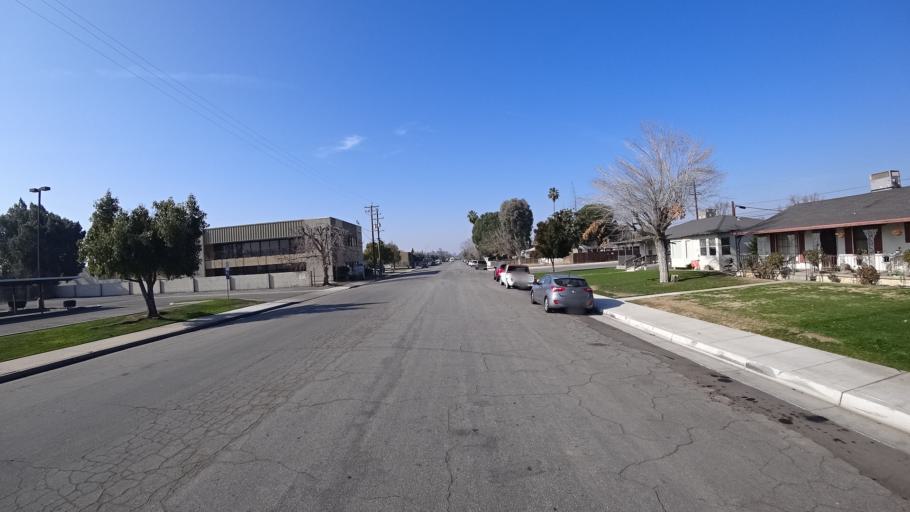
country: US
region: California
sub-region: Kern County
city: Bakersfield
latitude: 35.3724
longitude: -119.0311
